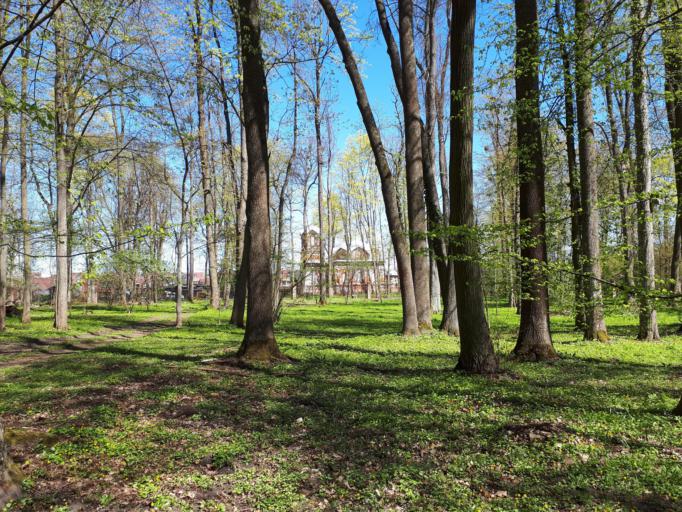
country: LT
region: Kauno apskritis
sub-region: Kaunas
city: Aleksotas
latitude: 54.8713
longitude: 23.9057
